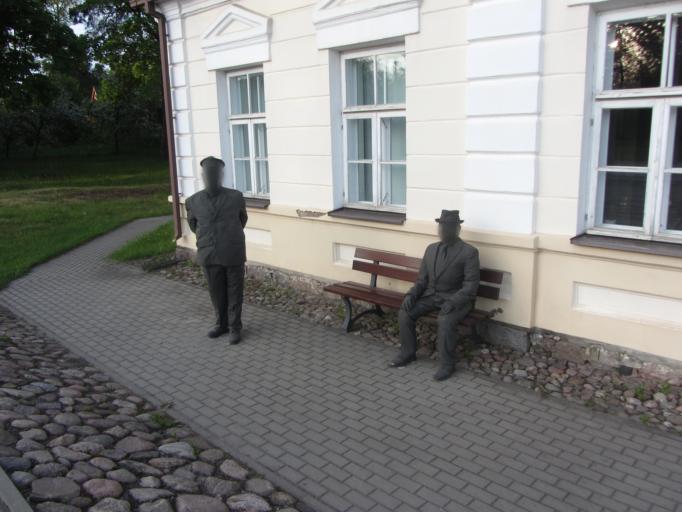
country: LT
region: Utenos apskritis
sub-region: Utena
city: Utena
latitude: 55.4942
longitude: 25.5819
